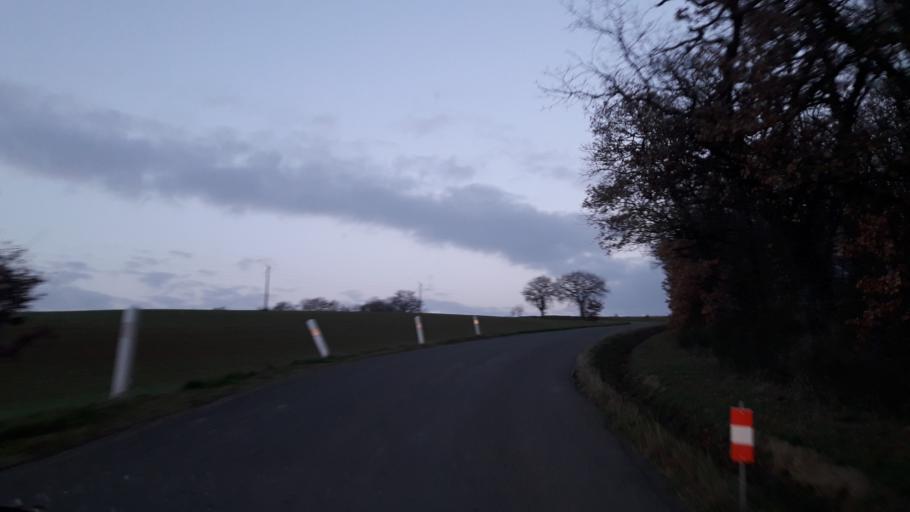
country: FR
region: Midi-Pyrenees
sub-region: Departement du Gers
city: Gimont
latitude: 43.6254
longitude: 0.9224
